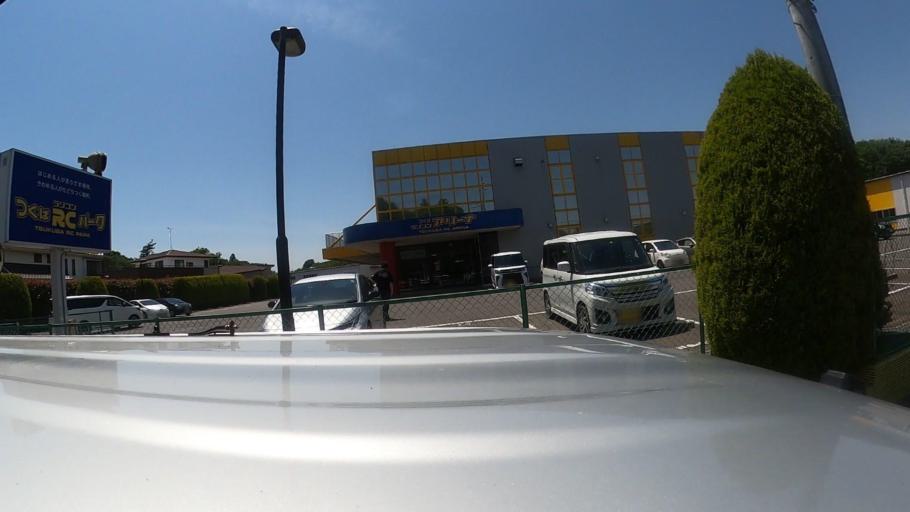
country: JP
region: Ibaraki
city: Ushiku
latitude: 36.0126
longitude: 140.0858
